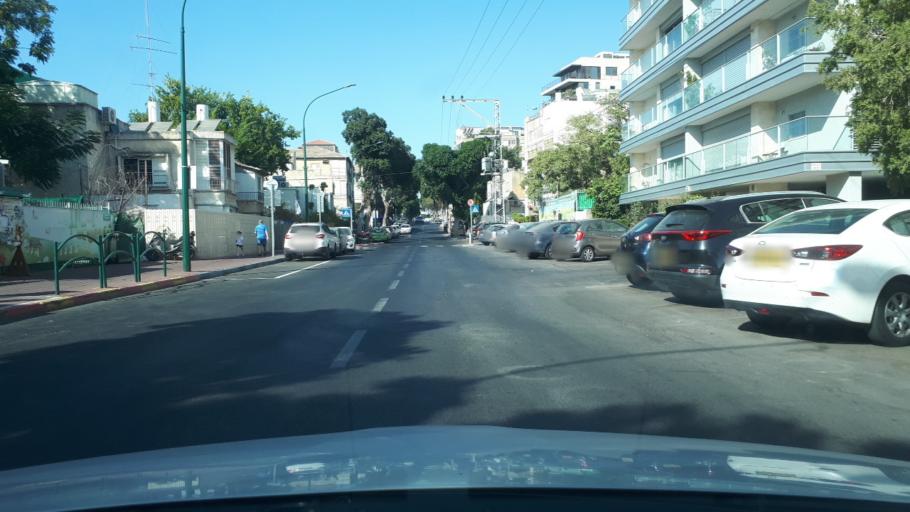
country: IL
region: Tel Aviv
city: Giv`atayim
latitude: 32.0689
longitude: 34.8220
